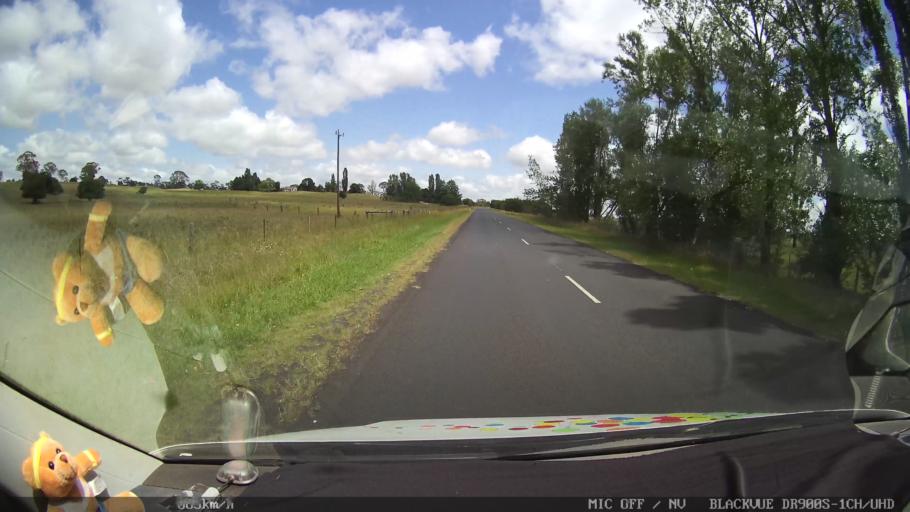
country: AU
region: New South Wales
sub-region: Glen Innes Severn
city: Glen Innes
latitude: -29.7062
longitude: 151.7206
